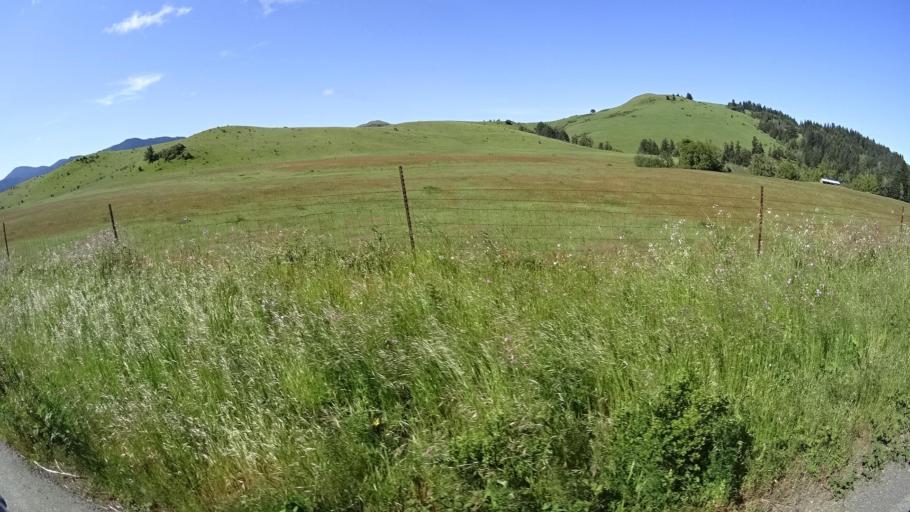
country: US
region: California
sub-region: Humboldt County
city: Ferndale
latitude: 40.3398
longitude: -124.3148
